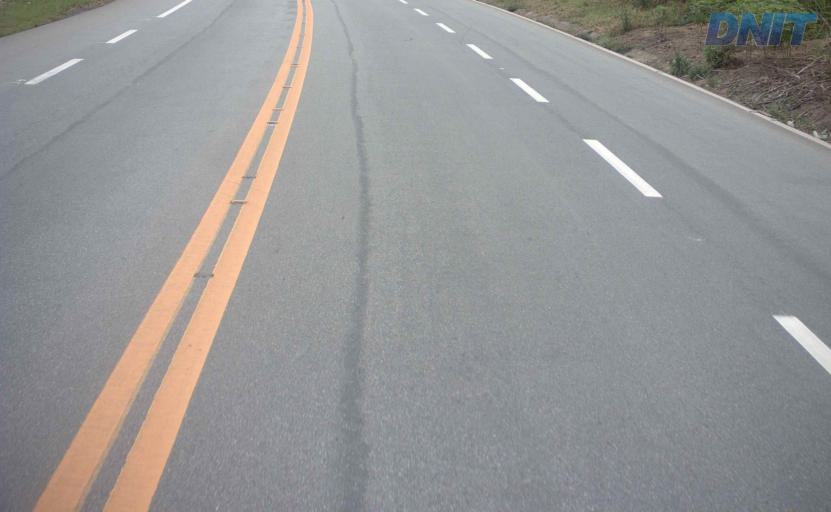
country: BR
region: Minas Gerais
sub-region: Timoteo
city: Timoteo
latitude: -19.6305
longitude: -42.8071
